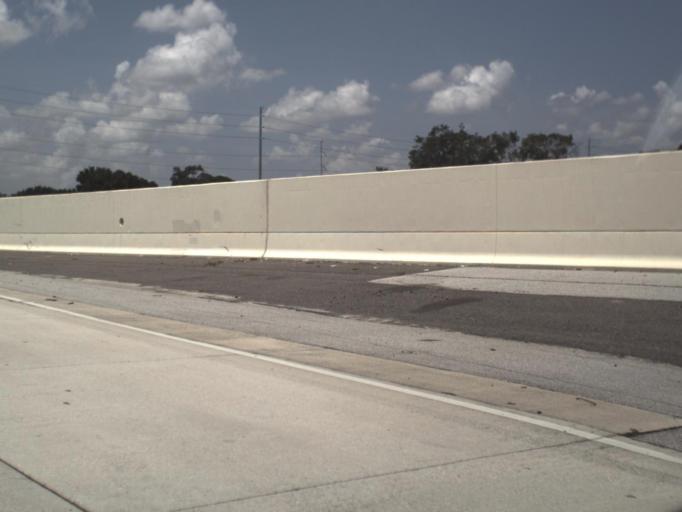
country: US
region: Florida
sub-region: Hillsborough County
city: Tampa
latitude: 27.9655
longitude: -82.4291
